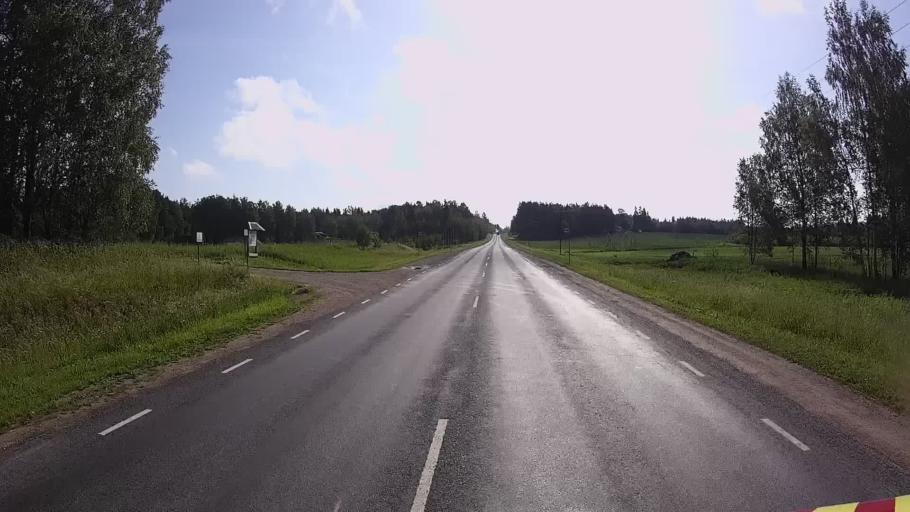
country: EE
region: Viljandimaa
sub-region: Viljandi linn
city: Viljandi
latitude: 58.3290
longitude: 25.5806
